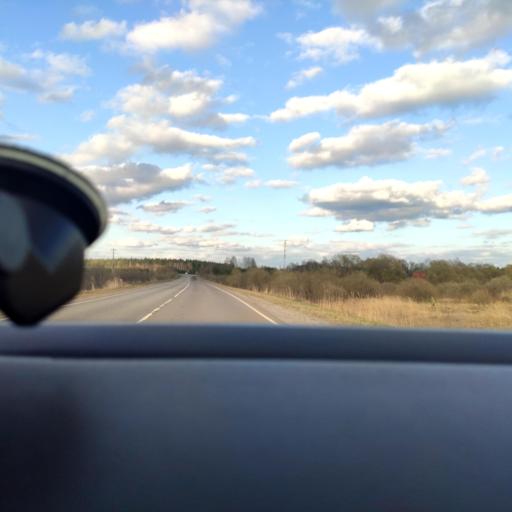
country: RU
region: Moskovskaya
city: Shaturtorf
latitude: 55.4342
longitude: 39.4170
